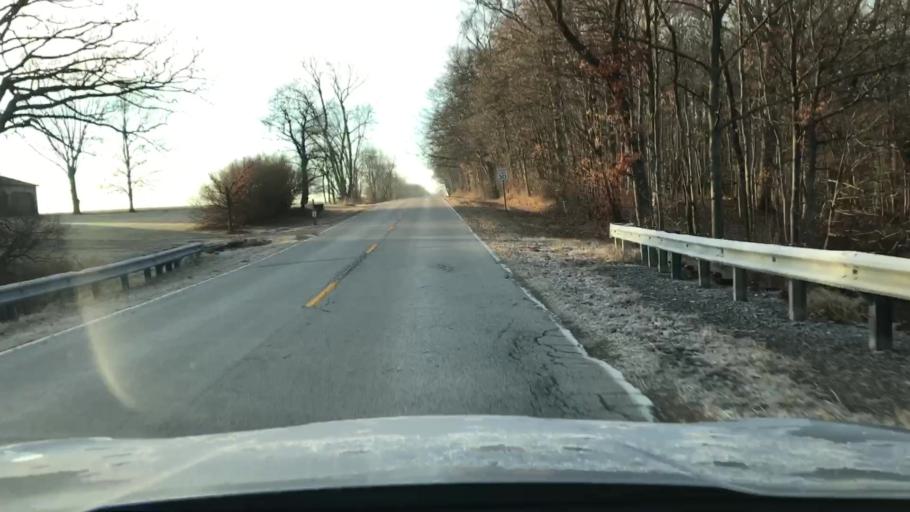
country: US
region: Illinois
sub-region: McLean County
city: Hudson
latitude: 40.6387
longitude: -88.9182
